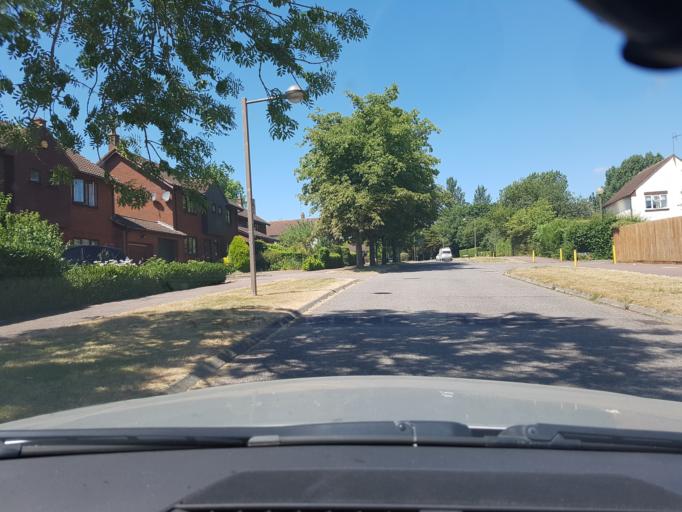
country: GB
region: England
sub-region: Milton Keynes
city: Bradwell
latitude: 52.0386
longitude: -0.8065
